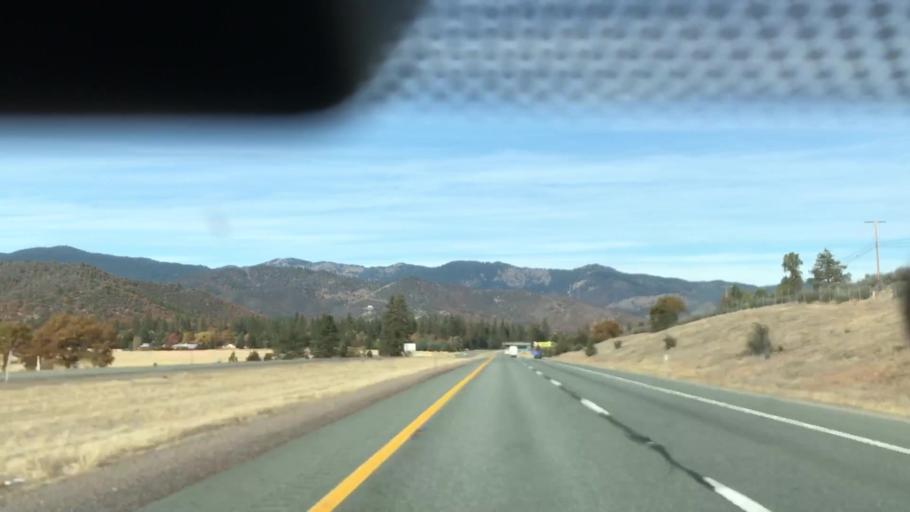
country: US
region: California
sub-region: Siskiyou County
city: Yreka
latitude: 41.6782
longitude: -122.6264
